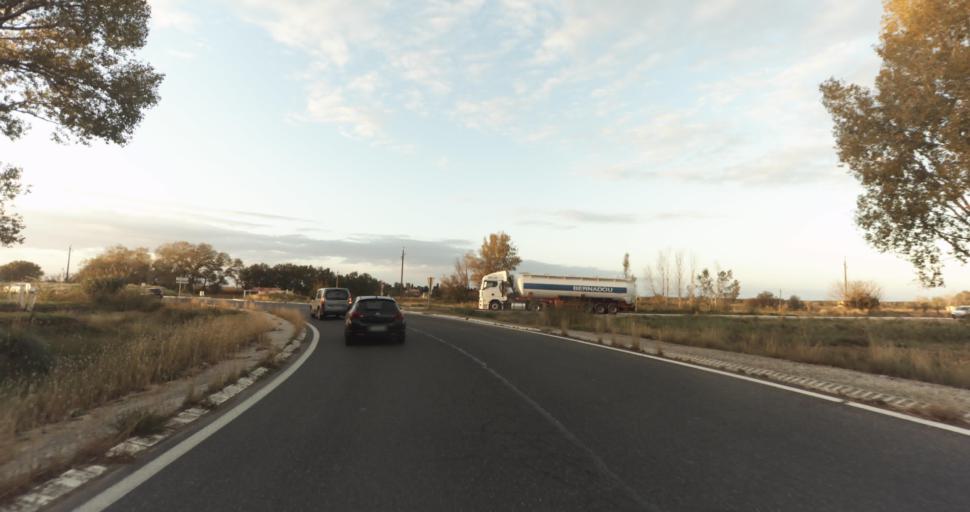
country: FR
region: Languedoc-Roussillon
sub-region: Departement du Gard
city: Le Grau-du-Roi
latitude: 43.5602
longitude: 4.1539
